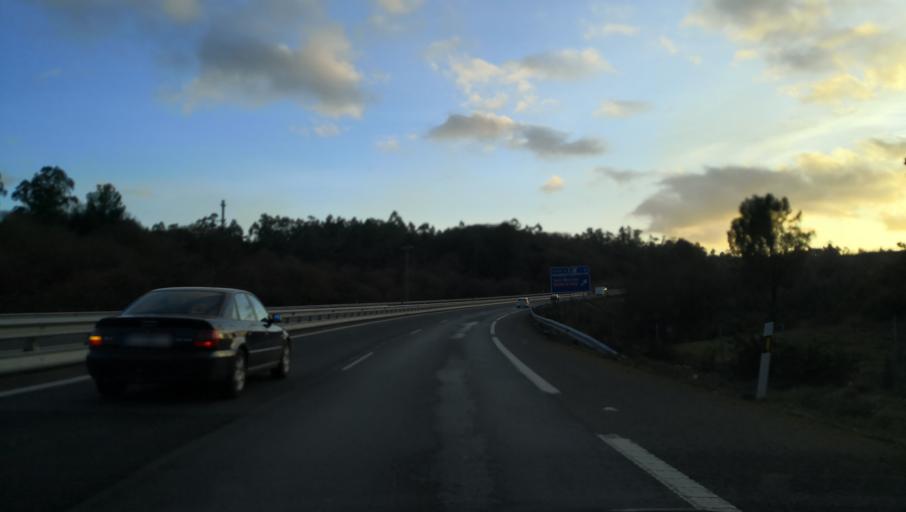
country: ES
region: Galicia
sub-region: Provincia da Coruna
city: Santiago de Compostela
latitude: 42.9002
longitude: -8.4682
